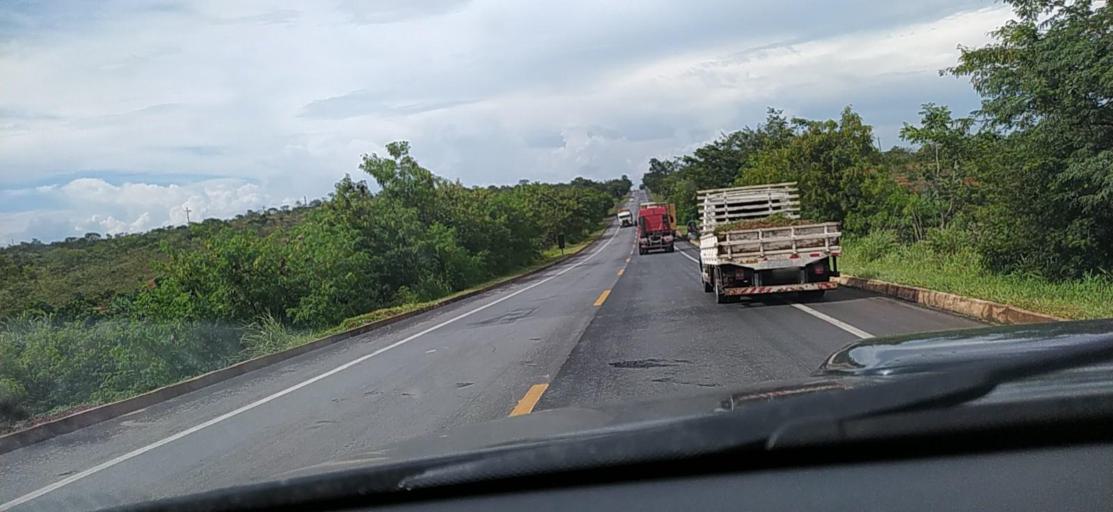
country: BR
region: Minas Gerais
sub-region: Montes Claros
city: Montes Claros
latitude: -16.8555
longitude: -43.8527
